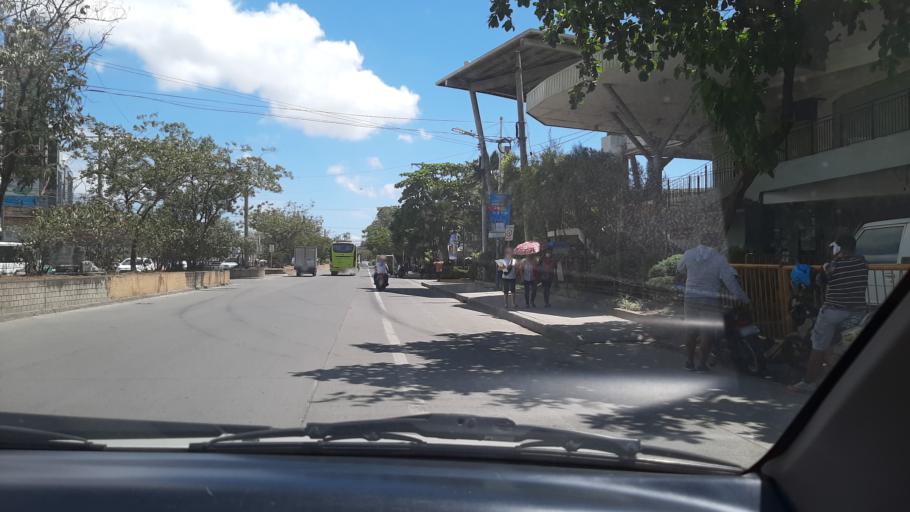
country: PH
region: Central Visayas
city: Mandaue City
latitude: 10.3256
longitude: 123.9333
